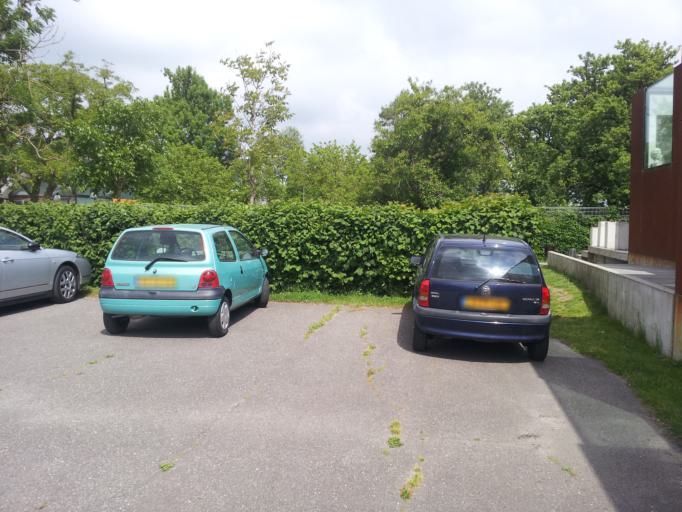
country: NL
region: South Holland
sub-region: Gemeente Delft
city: Delft
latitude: 51.9798
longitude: 4.3869
